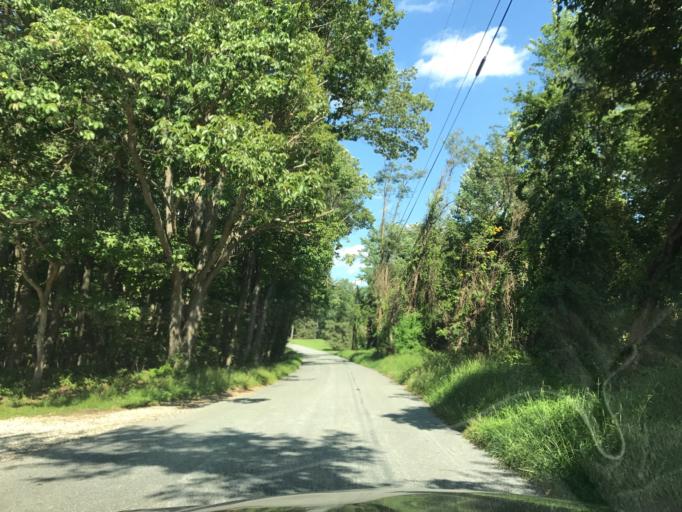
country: US
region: Maryland
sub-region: Baltimore County
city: Hunt Valley
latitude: 39.6072
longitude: -76.7045
